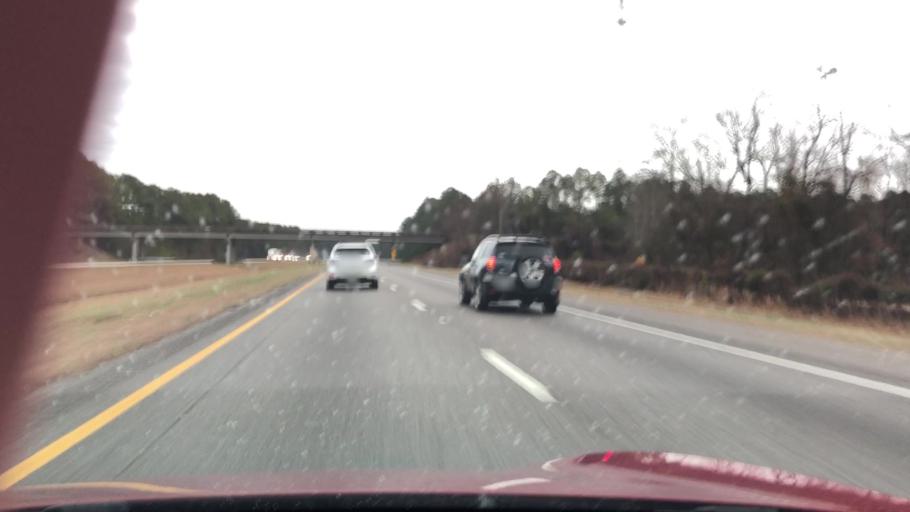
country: US
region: South Carolina
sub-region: Dillon County
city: Latta
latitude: 34.3313
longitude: -79.5634
